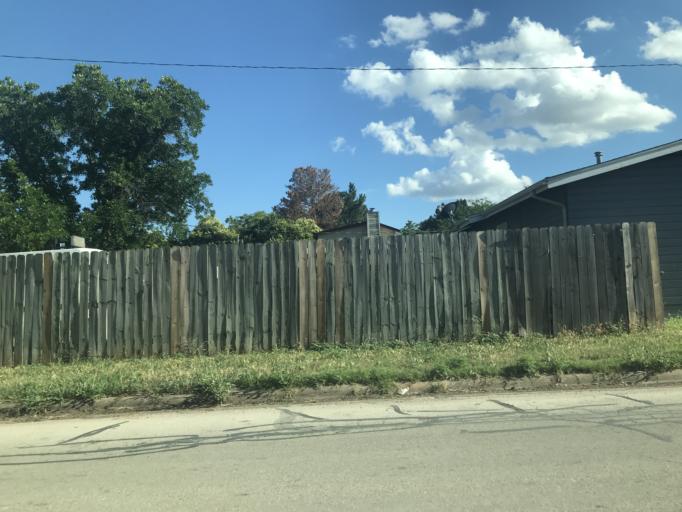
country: US
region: Texas
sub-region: Taylor County
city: Abilene
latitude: 32.4360
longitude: -99.7819
